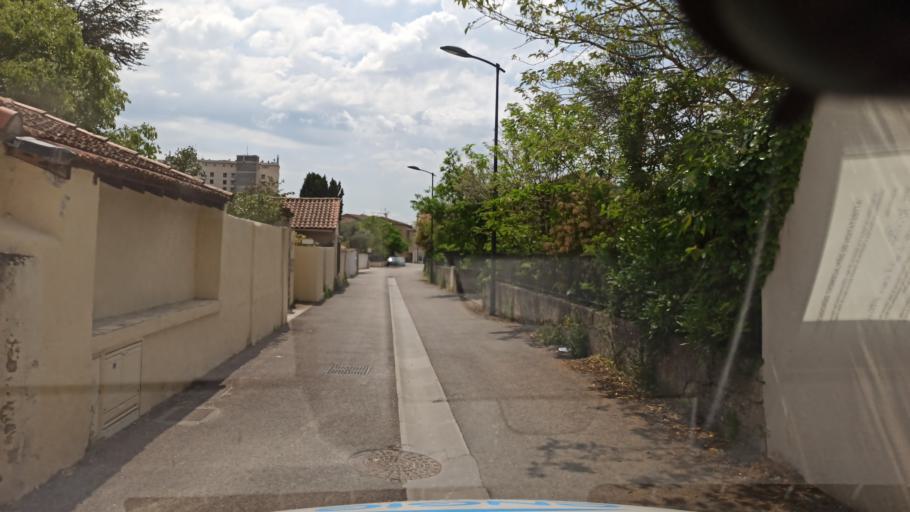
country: FR
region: Languedoc-Roussillon
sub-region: Departement du Gard
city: Les Angles
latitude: 43.9603
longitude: 4.7760
